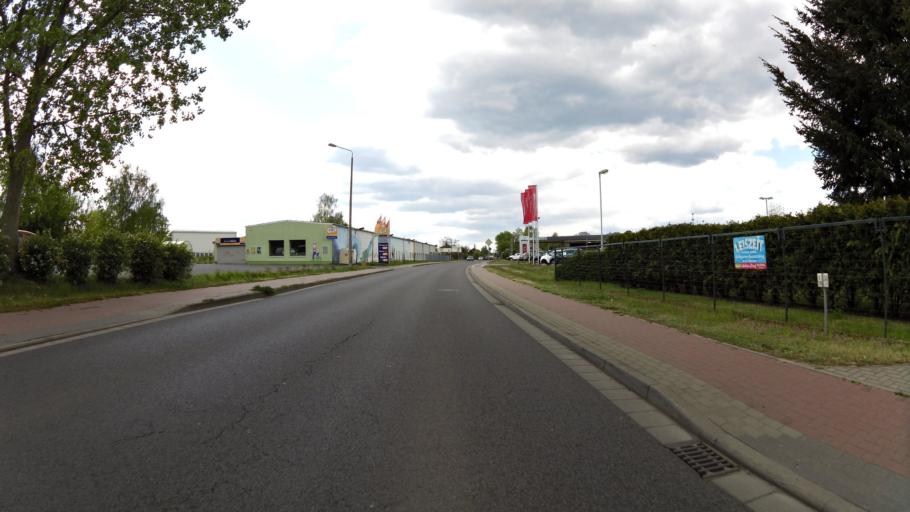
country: DE
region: Brandenburg
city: Furstenwalde
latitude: 52.3782
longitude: 14.0711
